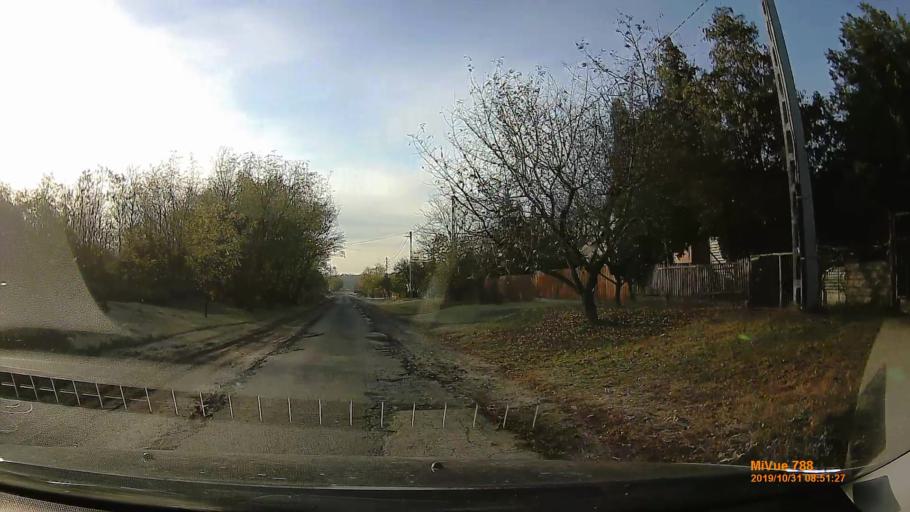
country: HU
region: Pest
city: Albertirsa
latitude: 47.2647
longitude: 19.6067
